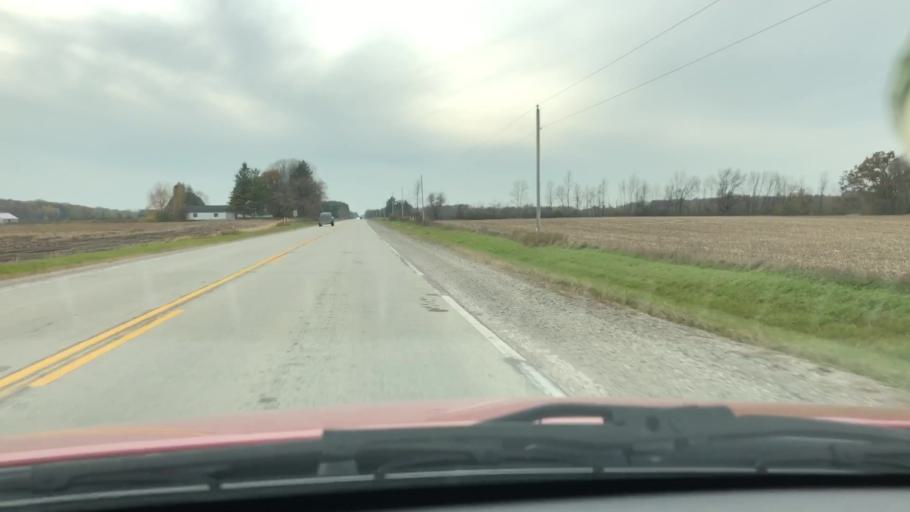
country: US
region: Wisconsin
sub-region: Brown County
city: Oneida
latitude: 44.4442
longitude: -88.1918
